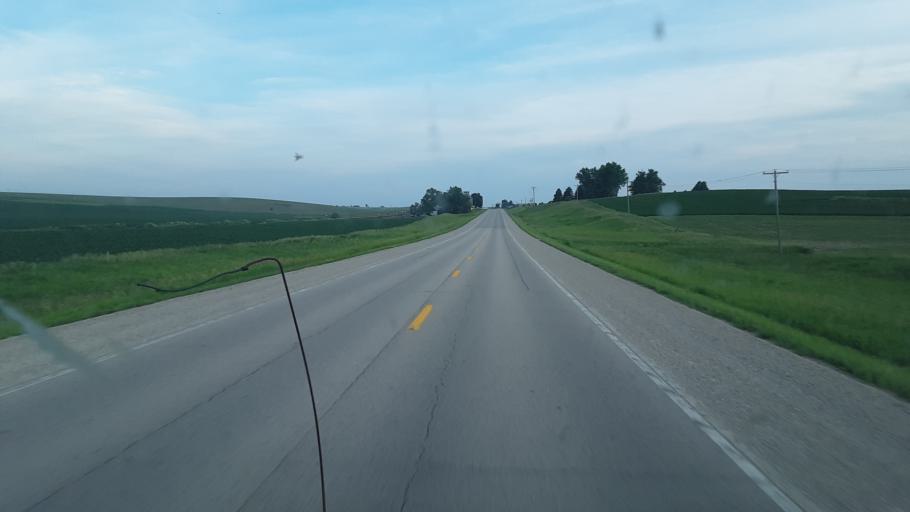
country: US
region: Iowa
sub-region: Benton County
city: Belle Plaine
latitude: 41.7830
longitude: -92.2793
